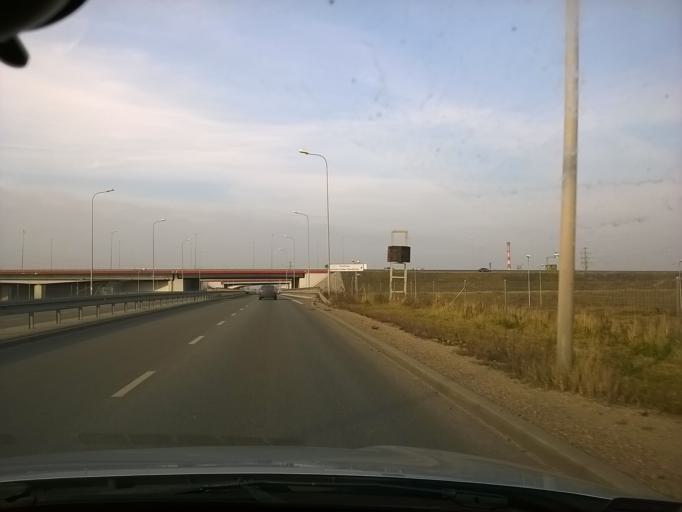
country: PL
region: Silesian Voivodeship
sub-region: Powiat gliwicki
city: Przyszowice
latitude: 50.2610
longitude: 18.7237
